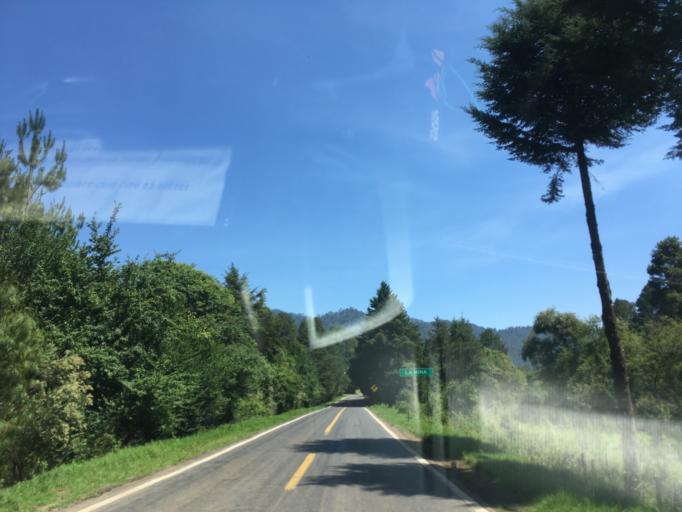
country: MX
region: Michoacan
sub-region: Hidalgo
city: Tierras Coloradas (San Pedro)
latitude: 19.6306
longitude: -100.7742
